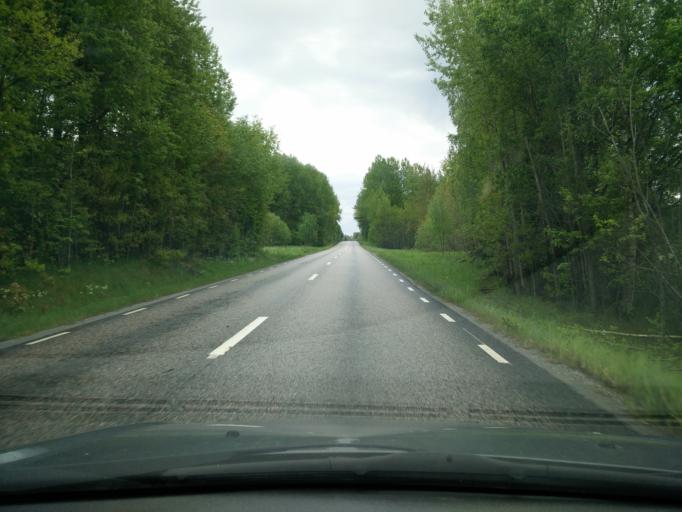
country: SE
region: Stockholm
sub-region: Norrtalje Kommun
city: Norrtalje
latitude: 59.7822
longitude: 18.7941
